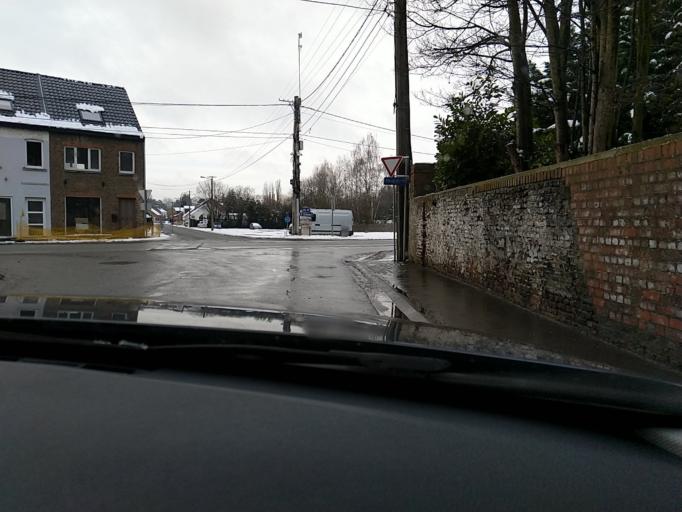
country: BE
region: Wallonia
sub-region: Province du Hainaut
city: Jurbise
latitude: 50.5102
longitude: 3.9264
